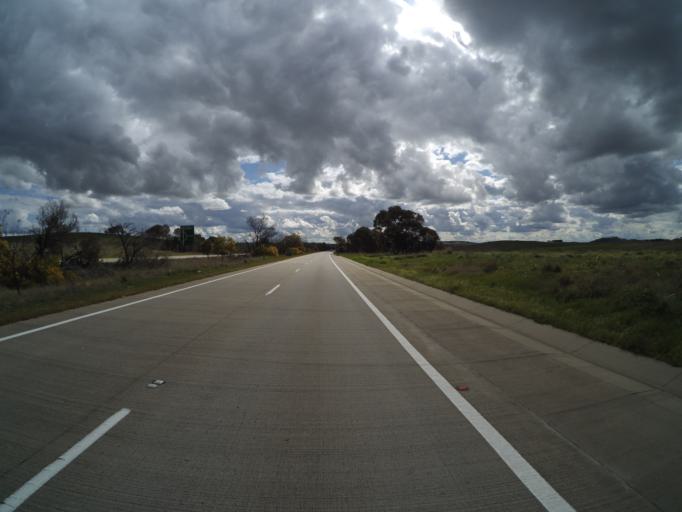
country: AU
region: New South Wales
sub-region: Yass Valley
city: Gundaroo
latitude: -34.7994
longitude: 149.2856
